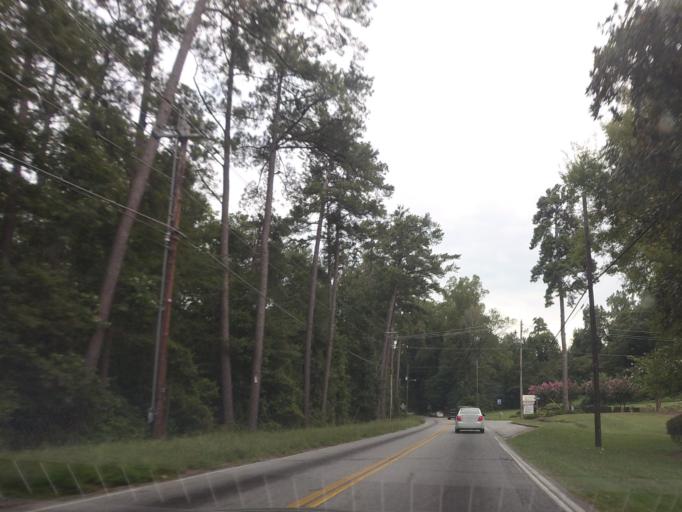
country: US
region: Georgia
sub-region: Bibb County
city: Macon
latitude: 32.8714
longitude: -83.6904
